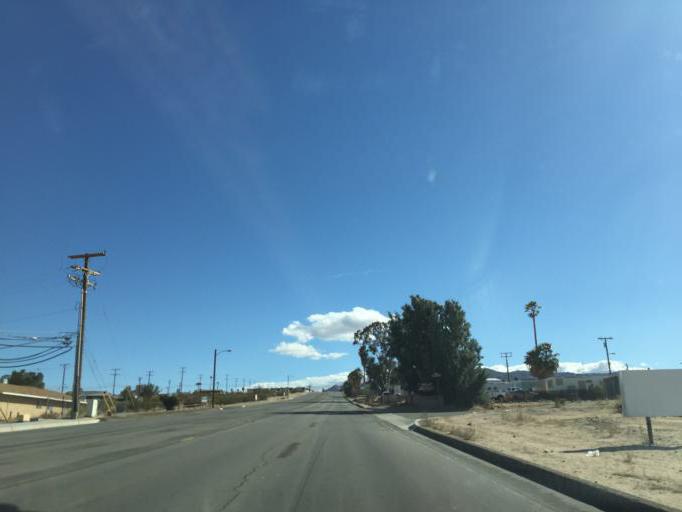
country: US
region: California
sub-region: San Bernardino County
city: Twentynine Palms
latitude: 34.1581
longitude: -116.0542
